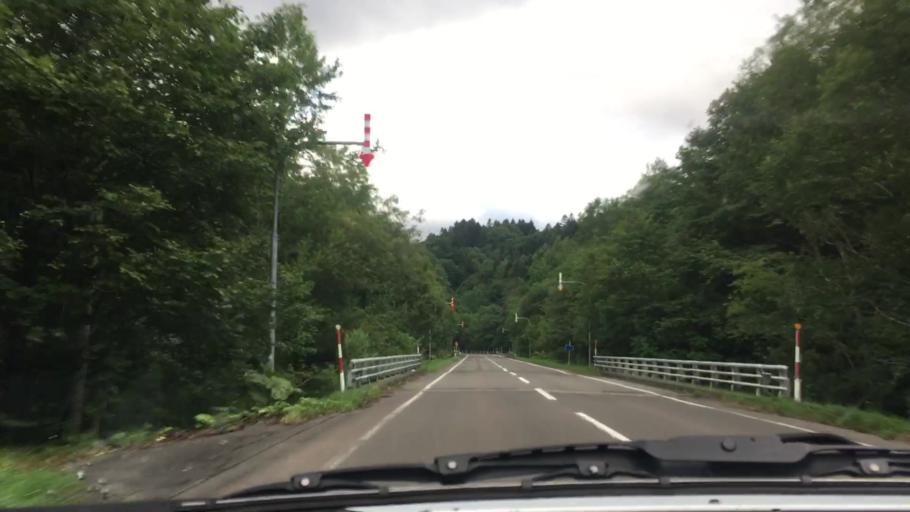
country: JP
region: Hokkaido
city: Shimo-furano
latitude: 43.0712
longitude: 142.6702
